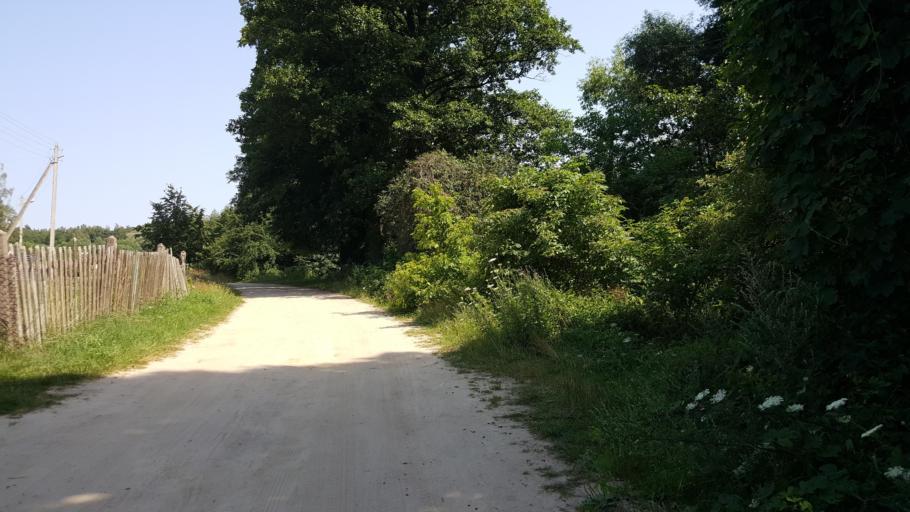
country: BY
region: Brest
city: Zhabinka
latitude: 52.1870
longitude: 24.0301
